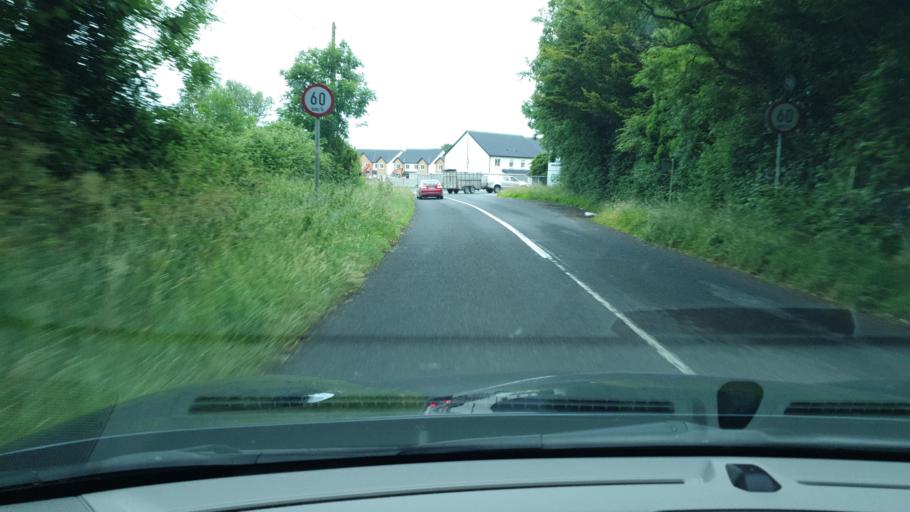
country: IE
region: Leinster
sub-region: An Mhi
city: Navan
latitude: 53.6477
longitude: -6.7085
